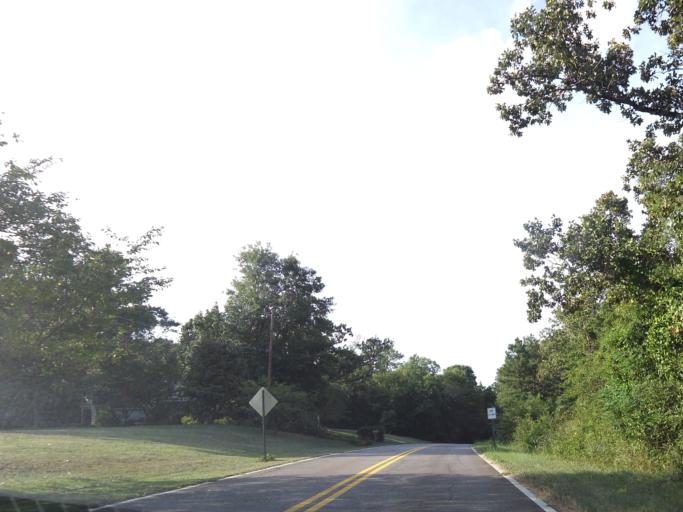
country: US
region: Georgia
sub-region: Houston County
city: Centerville
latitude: 32.7087
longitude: -83.6614
